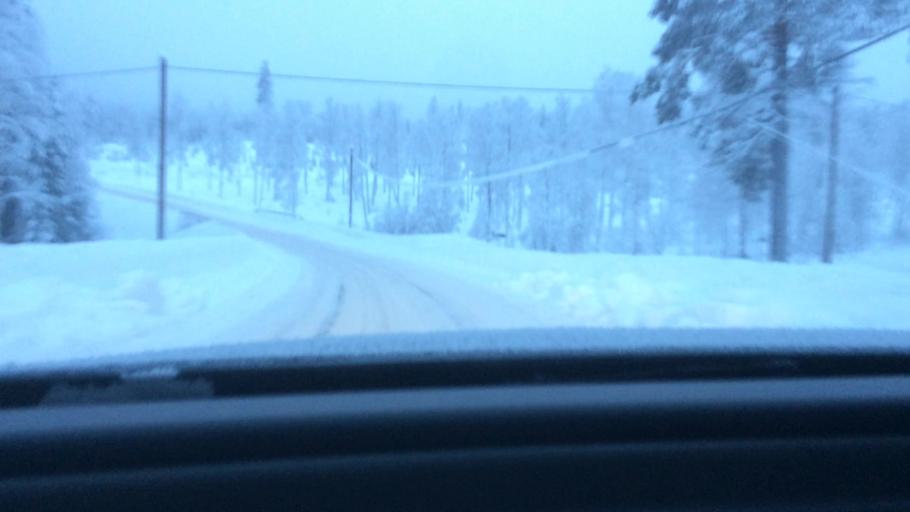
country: SE
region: Gaevleborg
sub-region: Ljusdals Kommun
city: Farila
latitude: 61.7643
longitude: 15.1497
